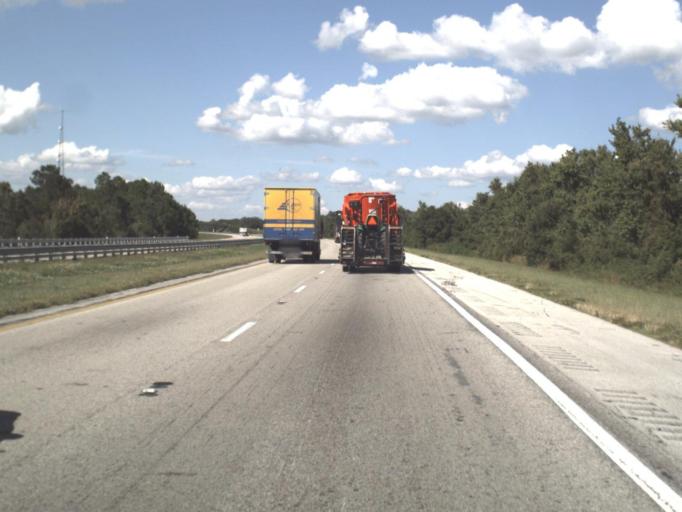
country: US
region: Florida
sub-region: Brevard County
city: June Park
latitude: 27.8596
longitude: -81.0097
